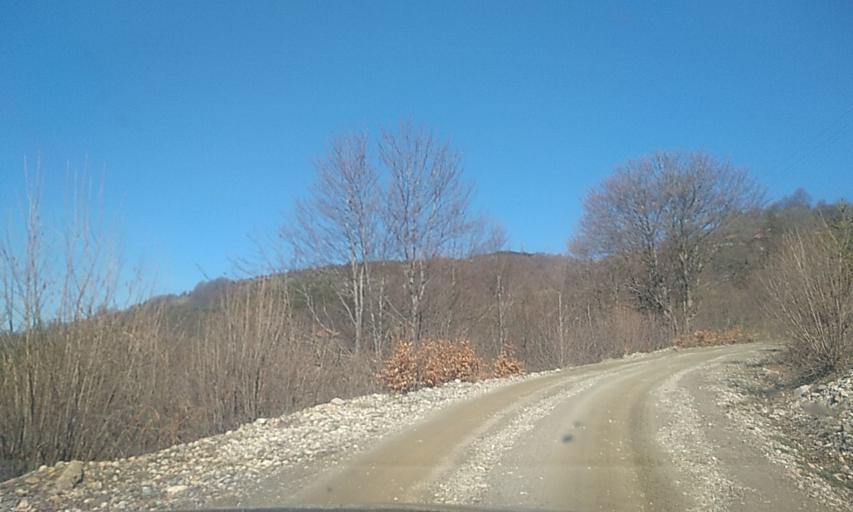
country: MK
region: Kriva Palanka
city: Kriva Palanka
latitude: 42.3437
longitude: 22.3499
